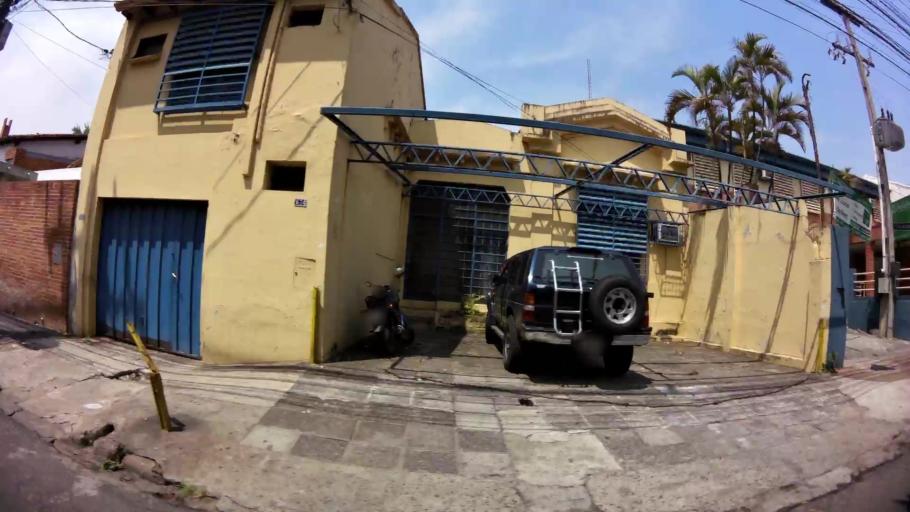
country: PY
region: Asuncion
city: Asuncion
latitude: -25.2854
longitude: -57.6095
